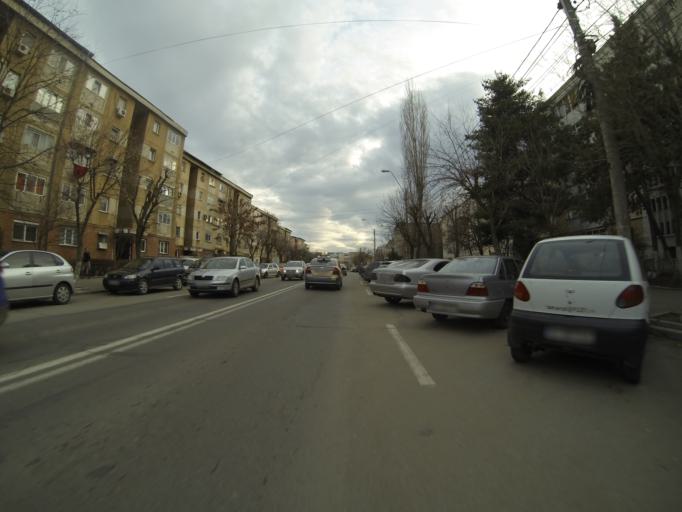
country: RO
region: Dolj
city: Craiova
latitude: 44.3079
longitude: 23.8211
